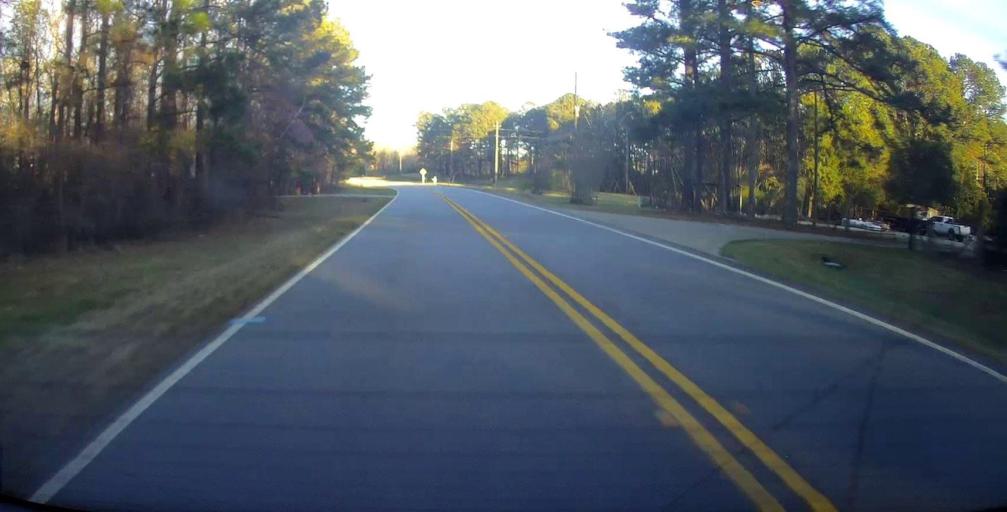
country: US
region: Georgia
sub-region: Harris County
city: Hamilton
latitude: 32.6729
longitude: -84.9372
